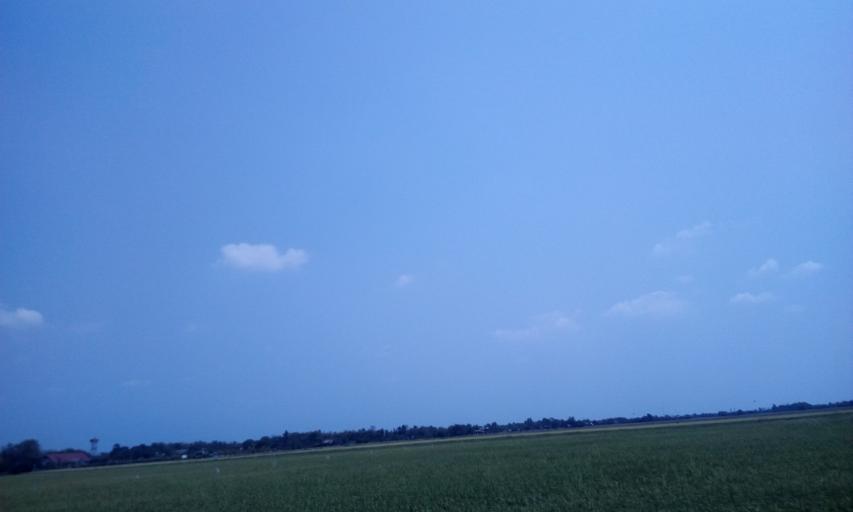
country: TH
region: Chachoengsao
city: Bang Nam Priao
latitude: 13.9643
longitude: 100.9663
